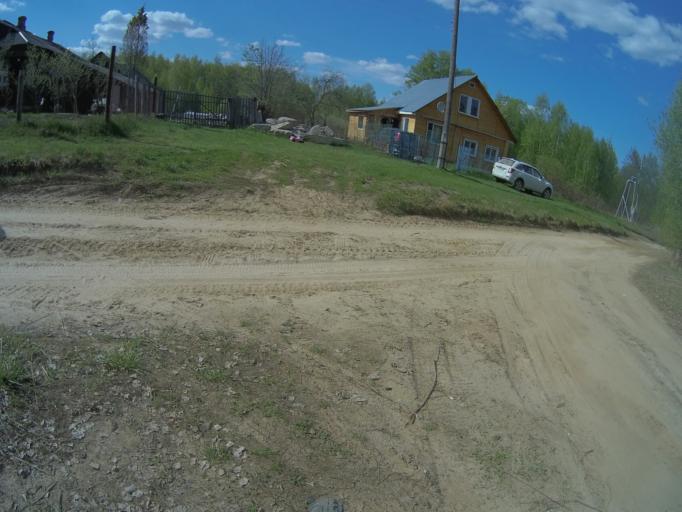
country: RU
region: Vladimir
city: Vorsha
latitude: 55.9713
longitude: 40.1660
